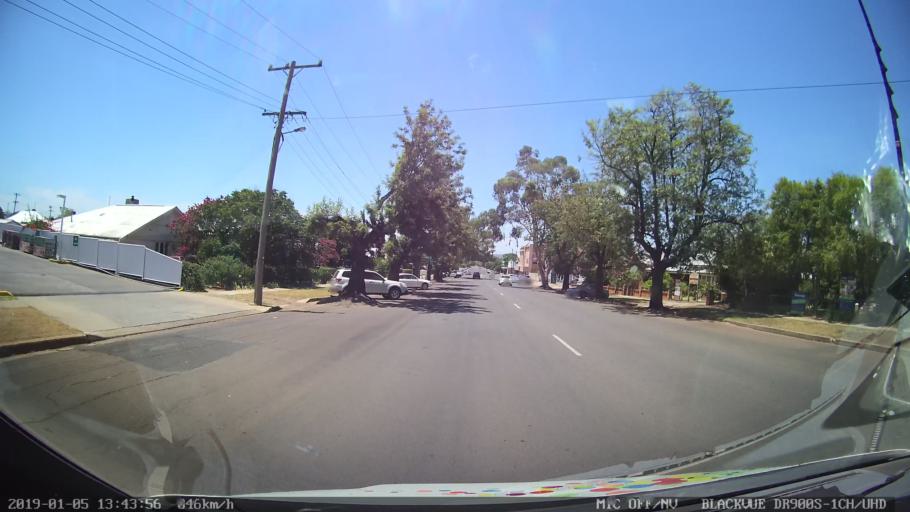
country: AU
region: New South Wales
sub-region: Gunnedah
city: Gunnedah
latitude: -30.9808
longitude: 150.2551
